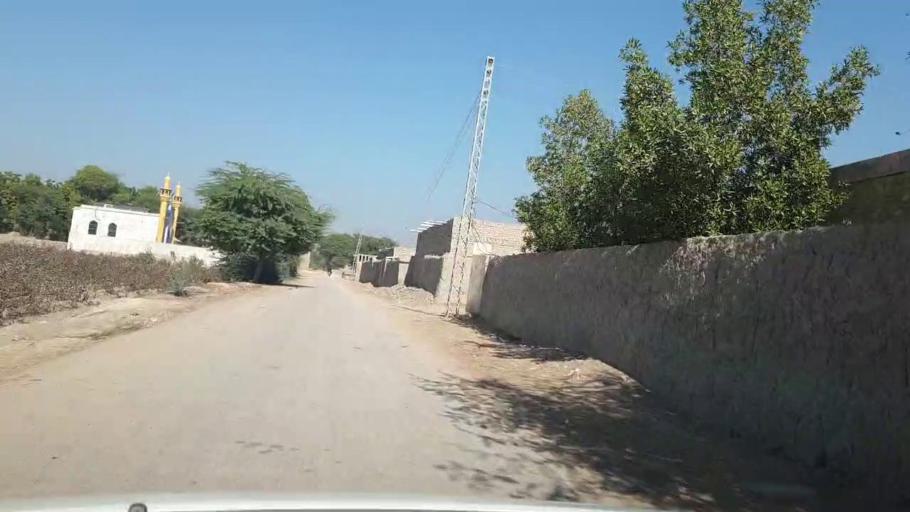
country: PK
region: Sindh
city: Johi
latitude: 26.6672
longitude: 67.7056
